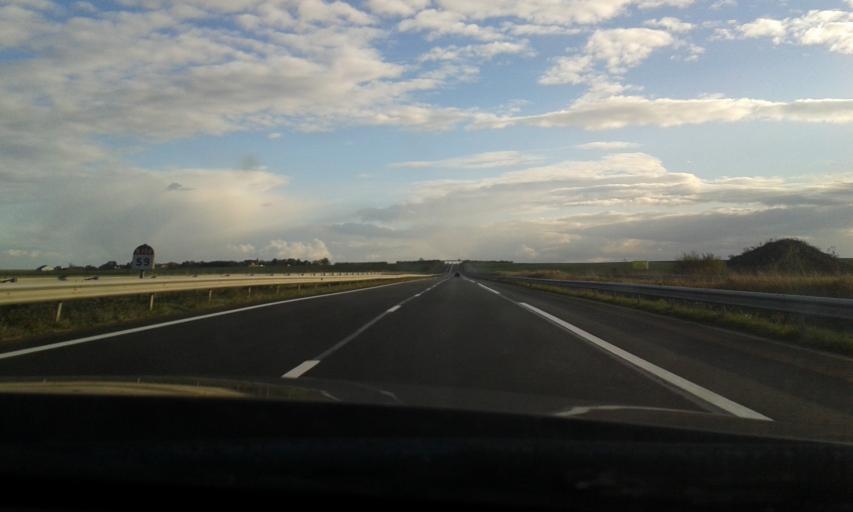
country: FR
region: Centre
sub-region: Departement d'Eure-et-Loir
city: Leves
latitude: 48.5211
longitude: 1.4576
